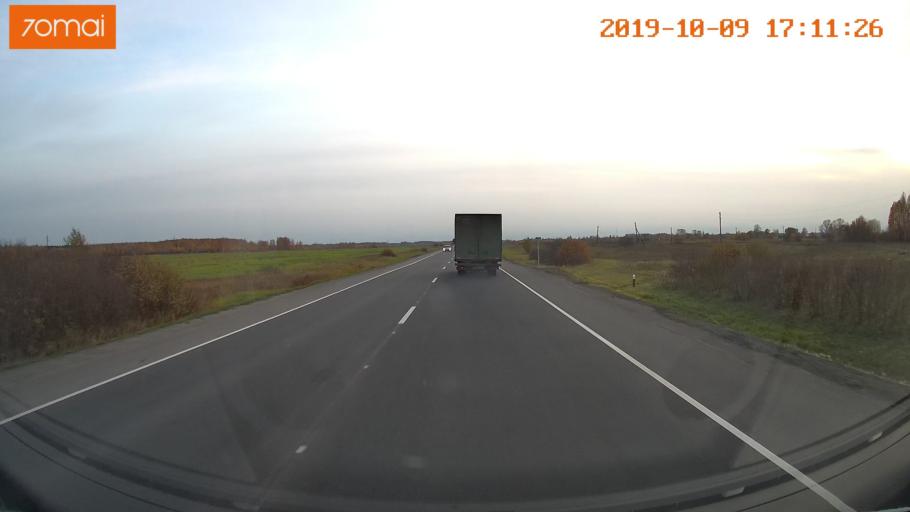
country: RU
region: Ivanovo
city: Privolzhsk
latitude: 57.3423
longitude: 41.2500
